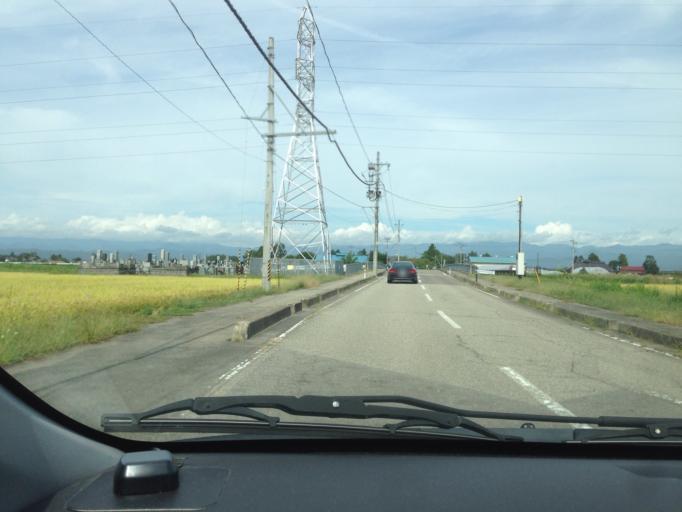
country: JP
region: Fukushima
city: Kitakata
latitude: 37.5752
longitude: 139.8881
